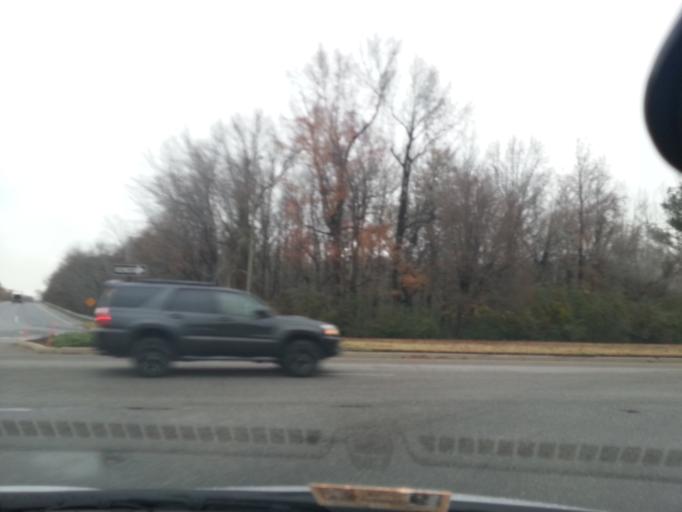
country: US
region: Virginia
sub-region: City of Chesapeake
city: Chesapeake
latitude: 36.7075
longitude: -76.2255
